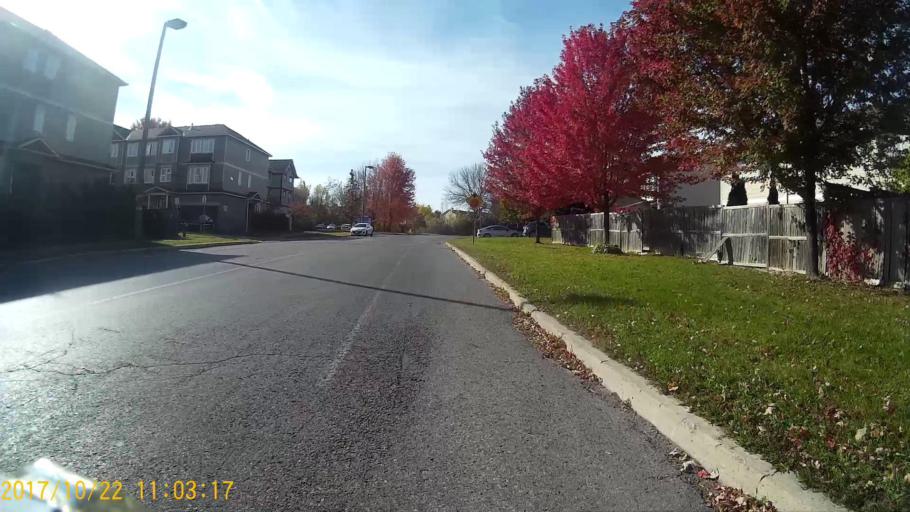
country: CA
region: Ontario
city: Bells Corners
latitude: 45.3537
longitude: -75.9226
